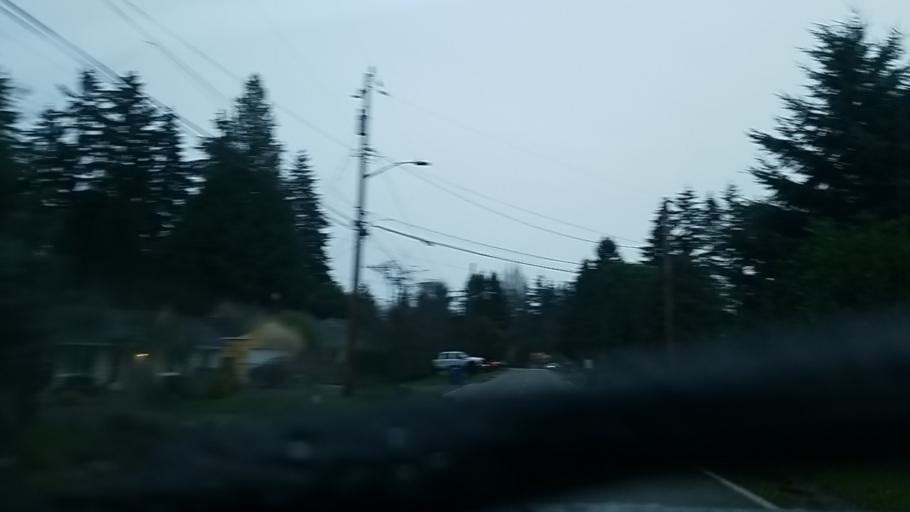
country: US
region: Washington
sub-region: King County
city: Shoreline
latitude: 47.7207
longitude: -122.3300
